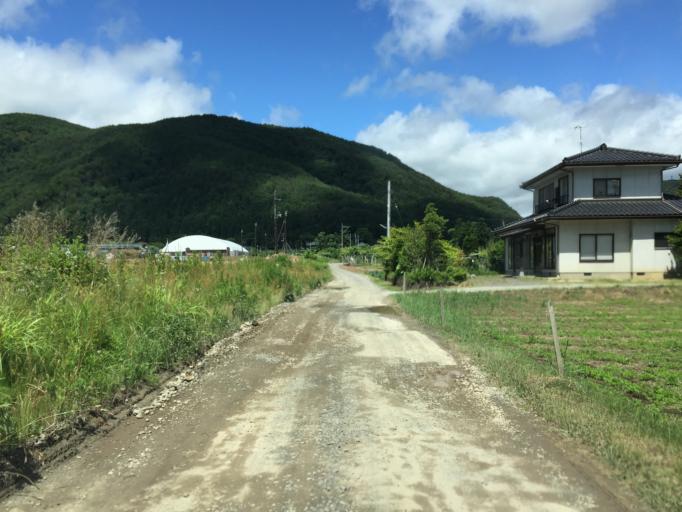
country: JP
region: Fukushima
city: Fukushima-shi
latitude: 37.8193
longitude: 140.4195
